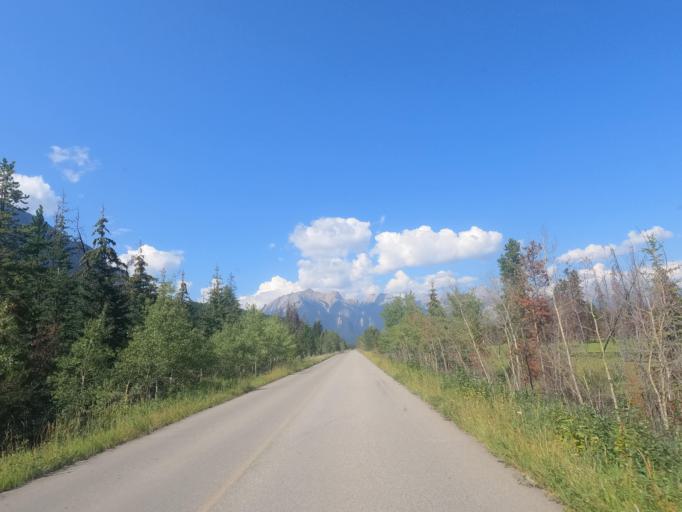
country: CA
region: Alberta
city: Jasper Park Lodge
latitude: 52.9795
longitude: -118.0700
